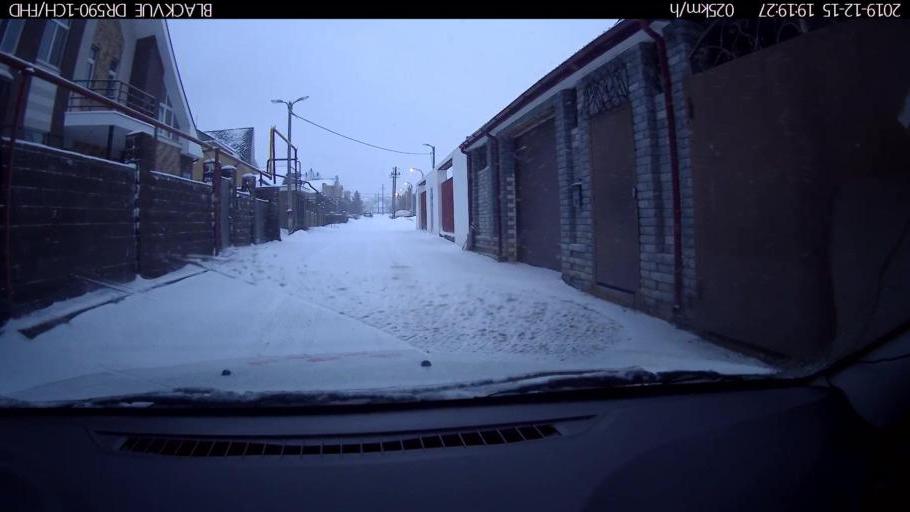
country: RU
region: Nizjnij Novgorod
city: Afonino
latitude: 56.3040
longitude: 44.0888
